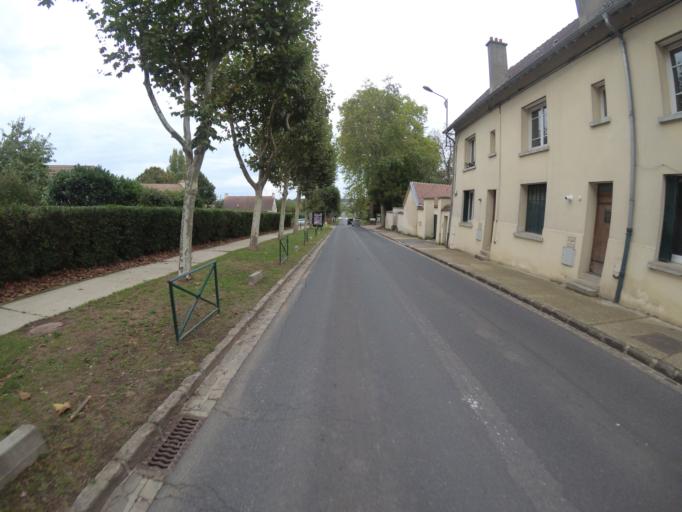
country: FR
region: Ile-de-France
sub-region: Departement de Seine-et-Marne
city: Torcy
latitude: 48.8504
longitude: 2.6655
